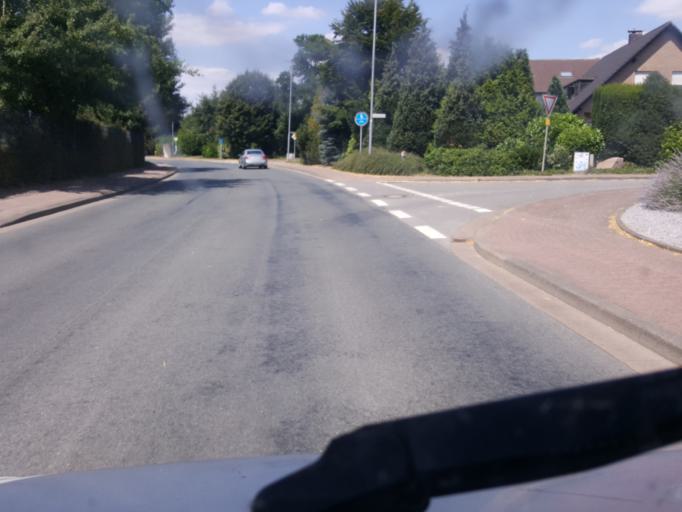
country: DE
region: North Rhine-Westphalia
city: Bad Oeynhausen
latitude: 52.2419
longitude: 8.7488
